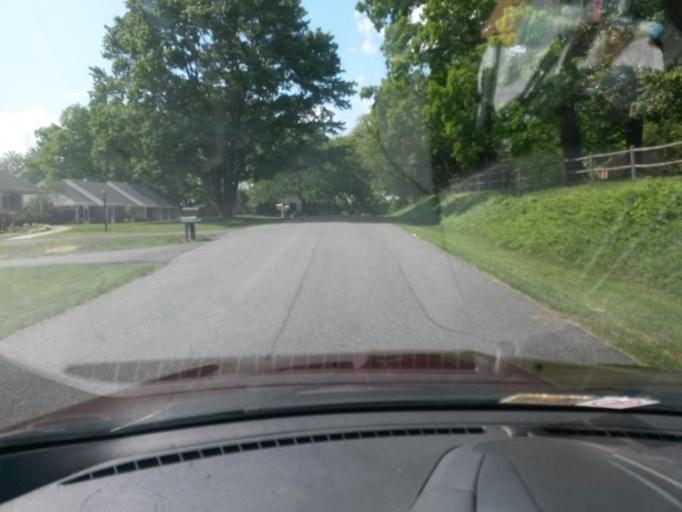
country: US
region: Virginia
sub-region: Campbell County
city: Timberlake
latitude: 37.3480
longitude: -79.2188
